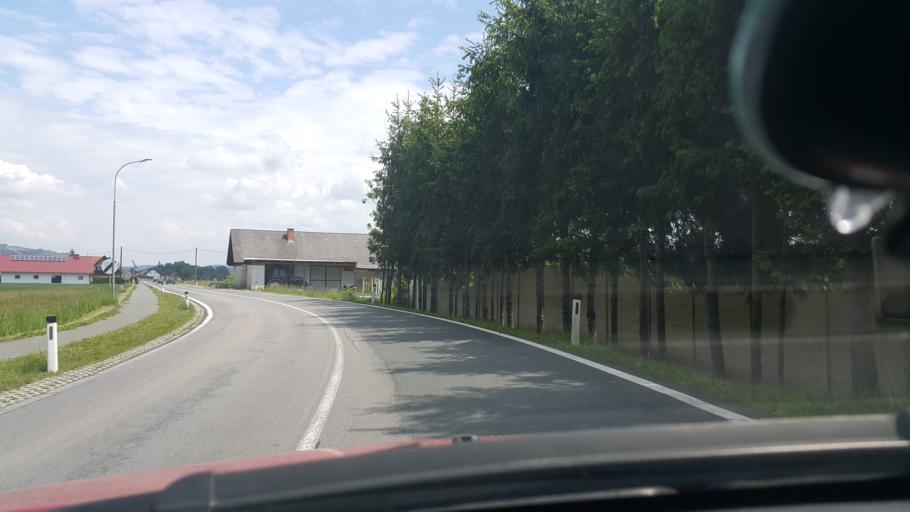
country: AT
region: Styria
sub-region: Politischer Bezirk Leibnitz
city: Gleinstatten
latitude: 46.7467
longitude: 15.3365
